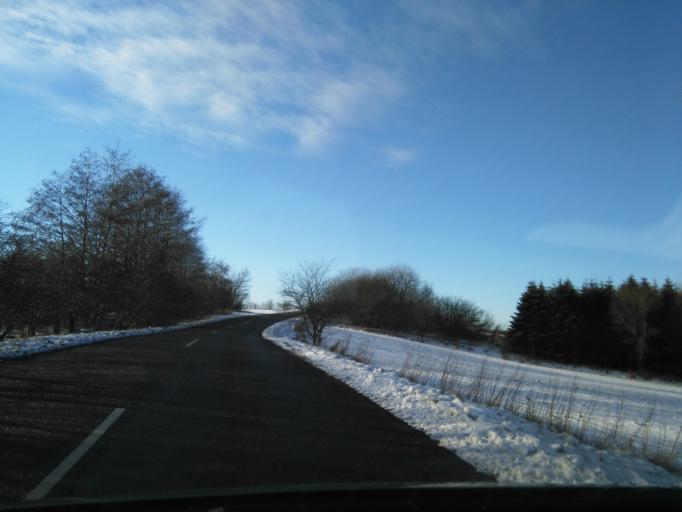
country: DK
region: Central Jutland
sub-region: Skanderborg Kommune
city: Skovby
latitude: 56.1194
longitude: 9.9857
